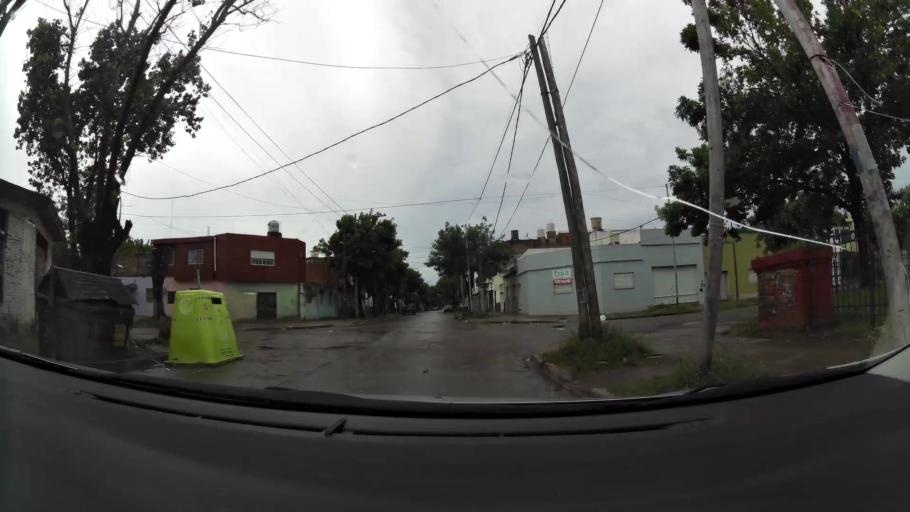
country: AR
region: Buenos Aires F.D.
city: Villa Lugano
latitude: -34.6603
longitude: -58.4476
